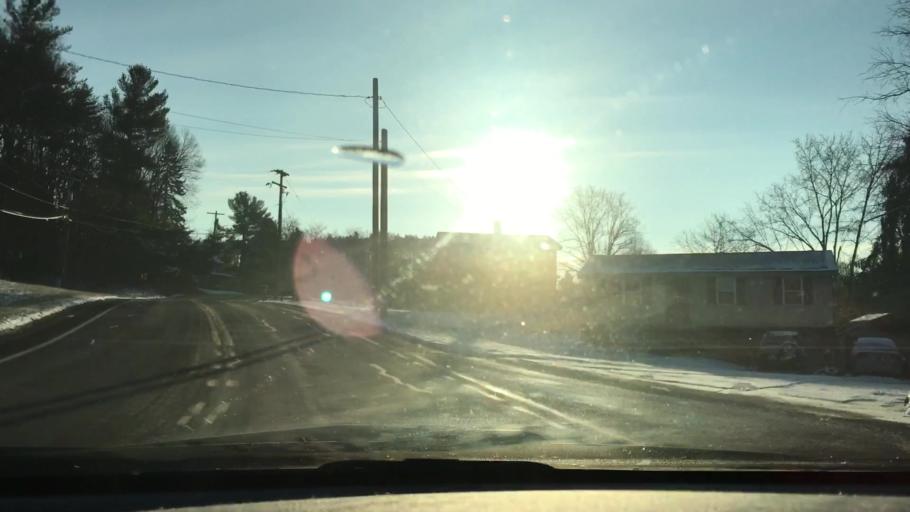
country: US
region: Pennsylvania
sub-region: Allegheny County
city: Elizabeth
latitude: 40.2606
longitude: -79.8501
